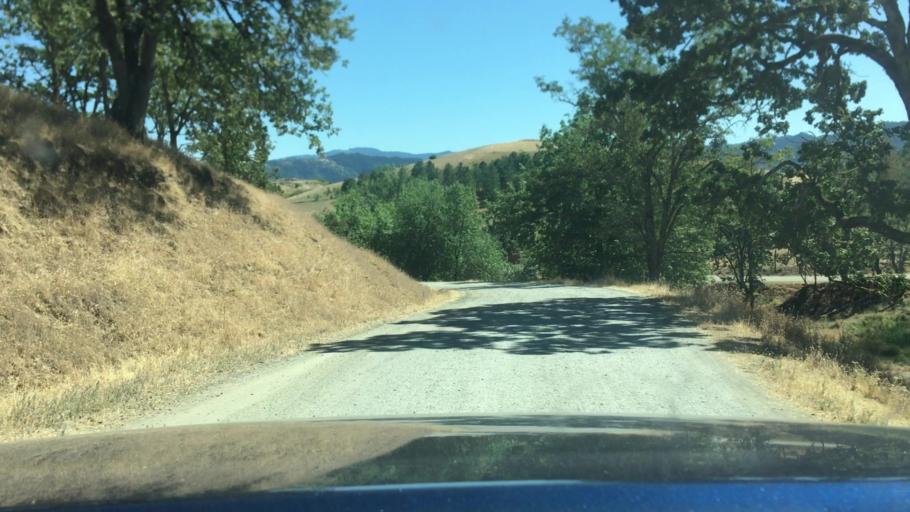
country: US
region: Oregon
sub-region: Douglas County
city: Winston
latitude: 43.1346
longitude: -123.4366
